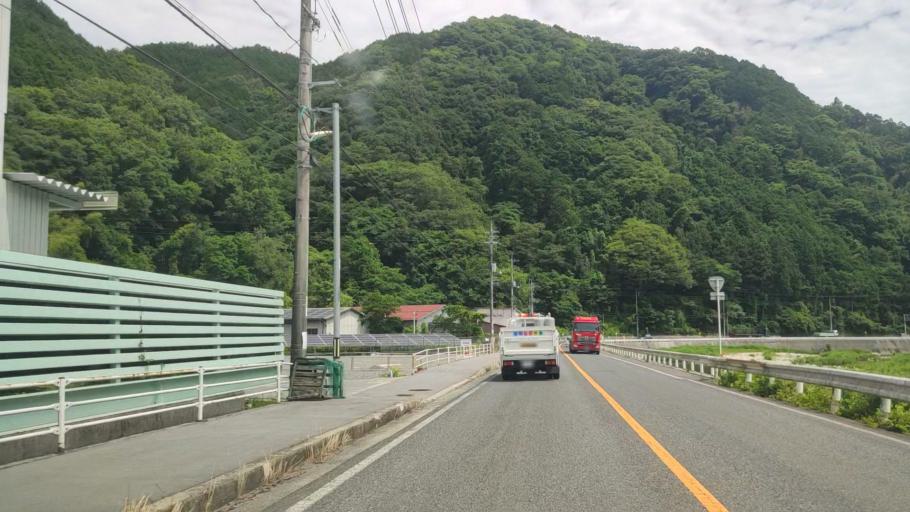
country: JP
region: Okayama
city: Niimi
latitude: 35.0730
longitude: 133.6804
